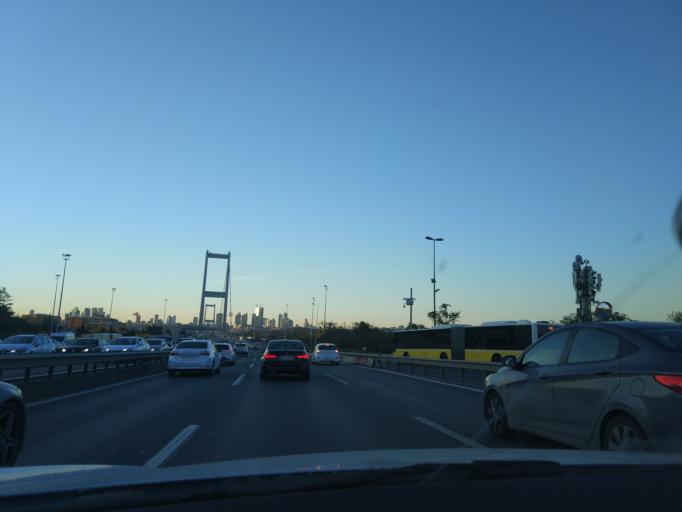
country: TR
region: Istanbul
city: UEskuedar
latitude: 41.0369
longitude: 29.0432
